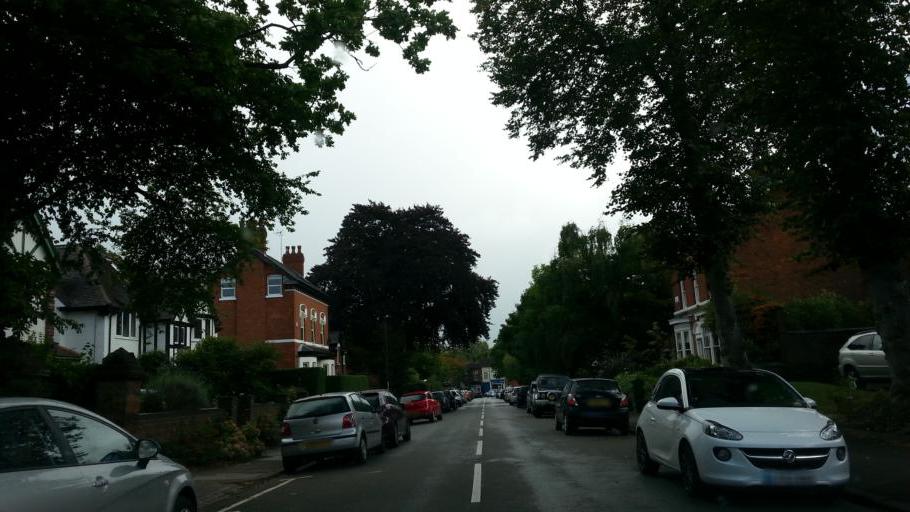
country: GB
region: England
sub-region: City and Borough of Birmingham
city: Birmingham
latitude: 52.4475
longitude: -1.9156
